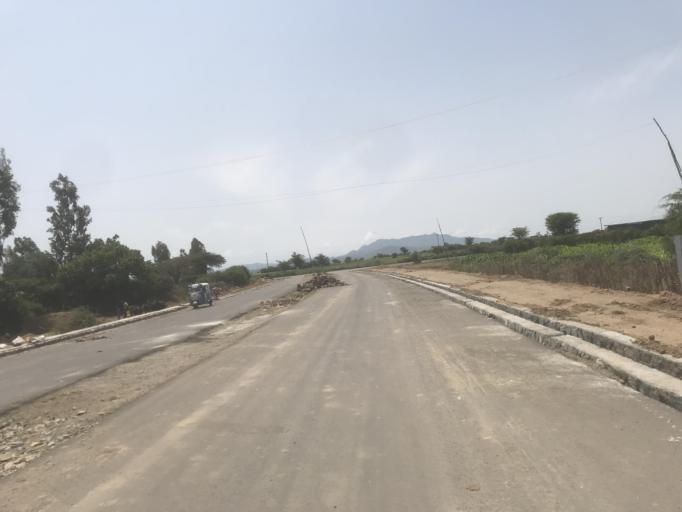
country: ET
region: Oromiya
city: Mojo
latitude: 8.2927
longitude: 38.9408
